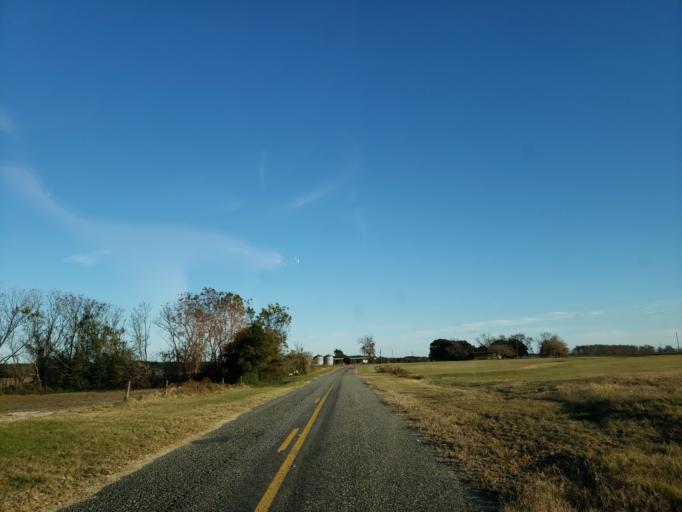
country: US
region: Georgia
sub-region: Dooly County
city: Unadilla
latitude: 32.1981
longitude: -83.7892
